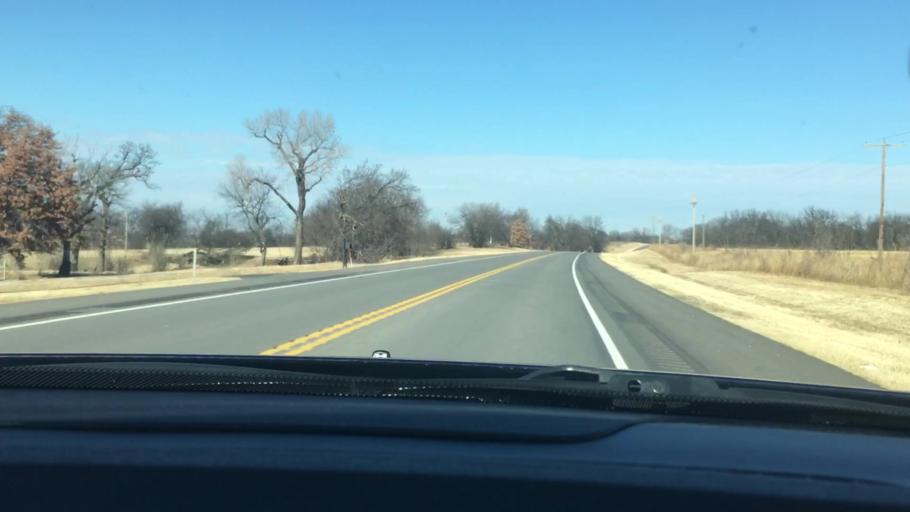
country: US
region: Oklahoma
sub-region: Murray County
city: Davis
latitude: 34.5479
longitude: -97.1318
